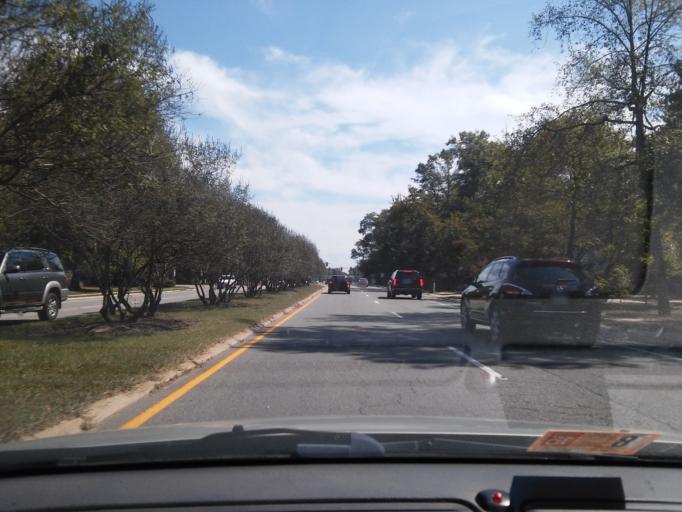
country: US
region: Virginia
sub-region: Chesterfield County
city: Bon Air
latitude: 37.5242
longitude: -77.6178
